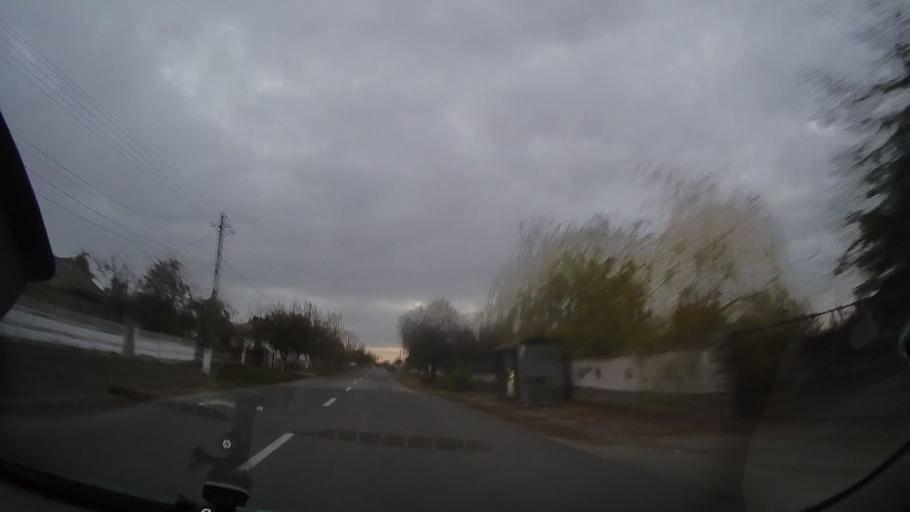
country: RO
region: Tulcea
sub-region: Comuna Mihai Bravu
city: Turda
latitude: 44.9746
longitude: 28.6233
